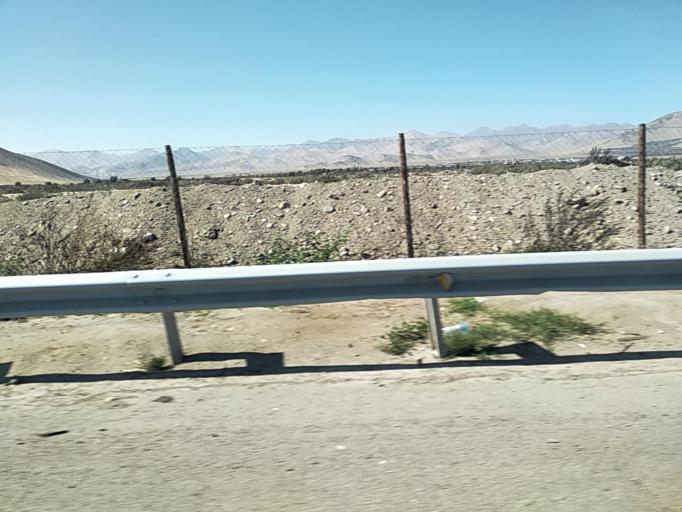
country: CL
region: Atacama
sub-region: Provincia de Copiapo
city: Copiapo
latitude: -27.3283
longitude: -70.3878
